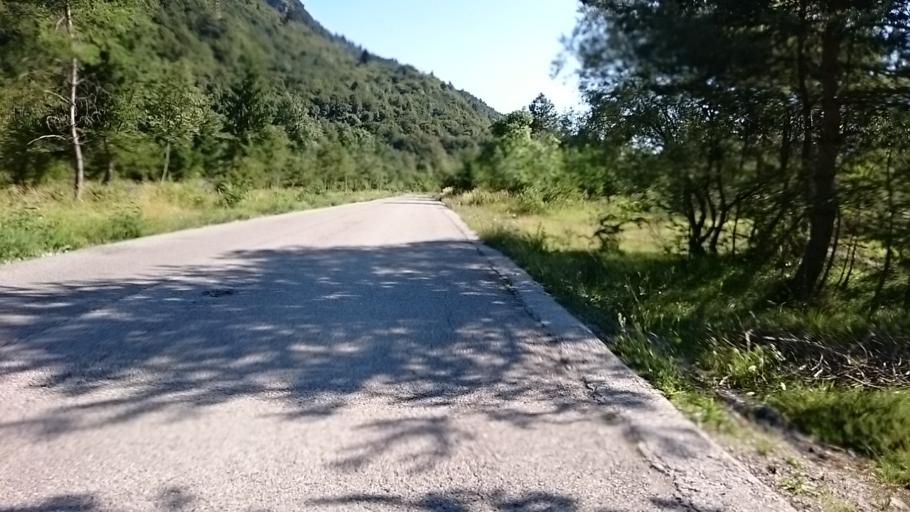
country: IT
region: Veneto
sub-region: Provincia di Belluno
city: Longarone
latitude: 46.2383
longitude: 12.3073
